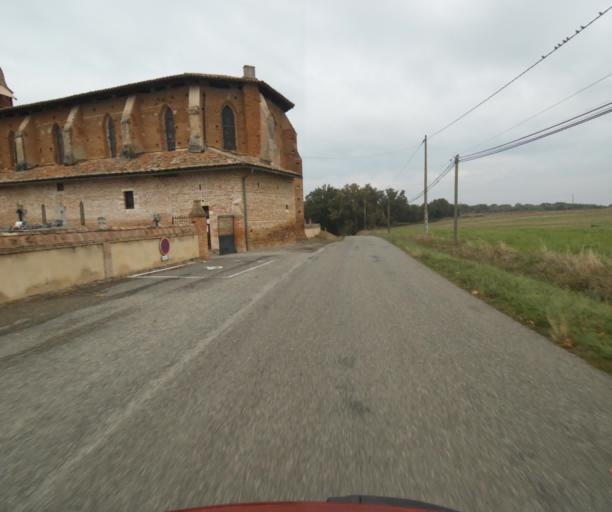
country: FR
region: Midi-Pyrenees
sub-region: Departement du Tarn-et-Garonne
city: Verdun-sur-Garonne
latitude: 43.8347
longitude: 1.1954
